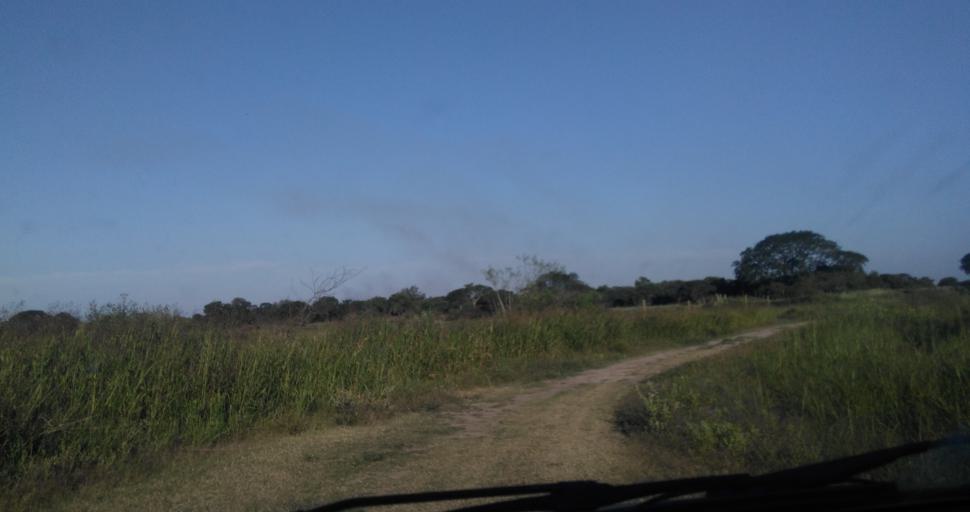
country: AR
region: Chaco
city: Fontana
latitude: -27.4266
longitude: -59.0572
